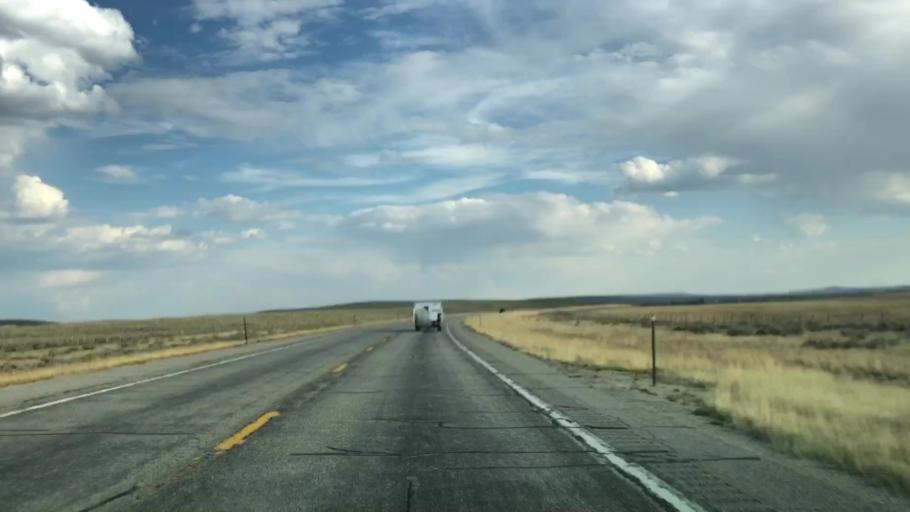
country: US
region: Wyoming
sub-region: Sublette County
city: Pinedale
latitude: 43.0335
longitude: -110.1300
